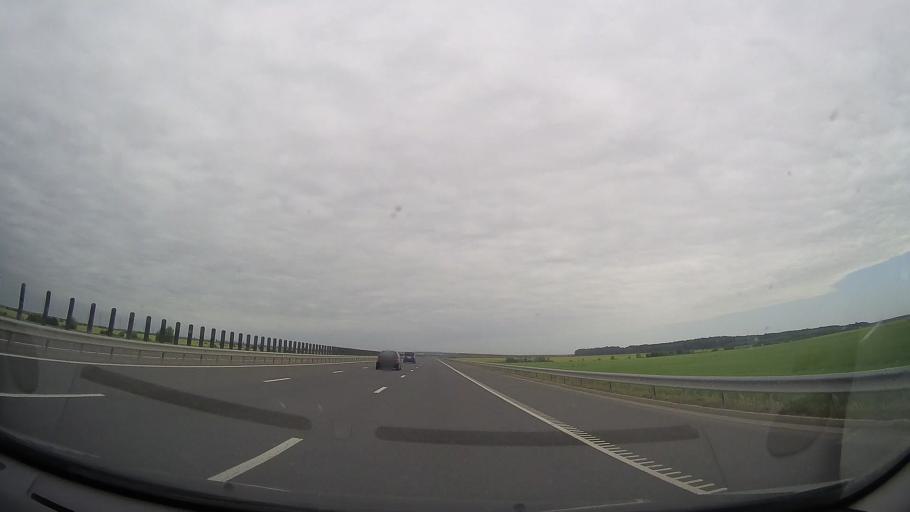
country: RO
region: Ilfov
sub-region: Comuna Moara Vlasiei
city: Caciulati
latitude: 44.5842
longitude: 26.1783
